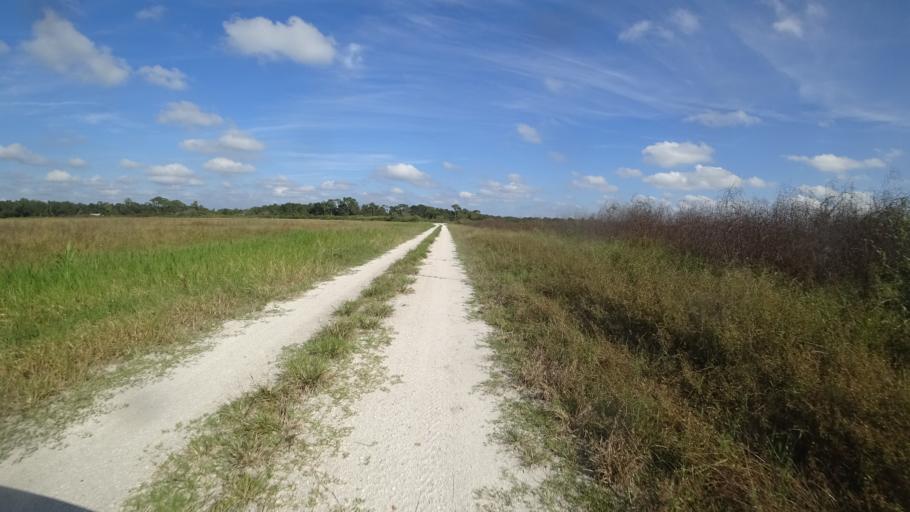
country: US
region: Florida
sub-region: Sarasota County
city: Lake Sarasota
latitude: 27.3724
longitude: -82.1590
